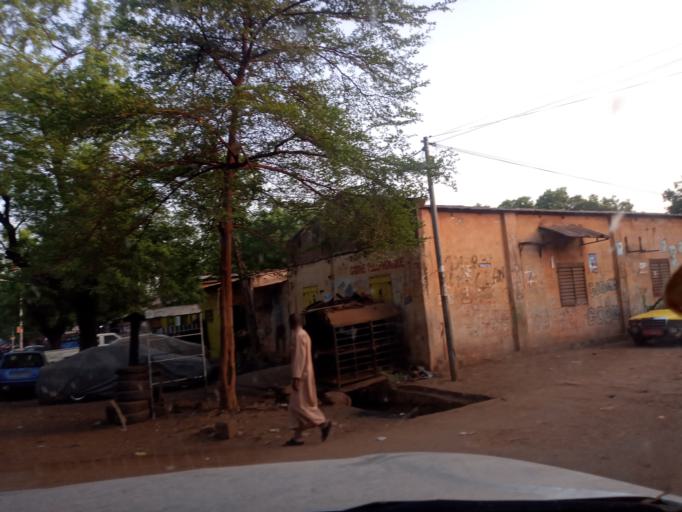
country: ML
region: Bamako
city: Bamako
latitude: 12.6583
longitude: -7.9836
